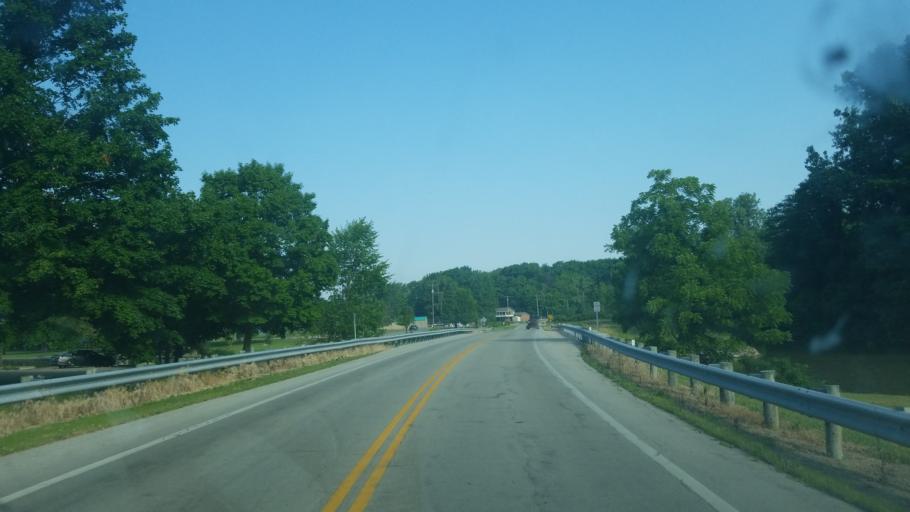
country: US
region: Ohio
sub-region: Logan County
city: Russells Point
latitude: 40.4788
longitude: -83.8596
